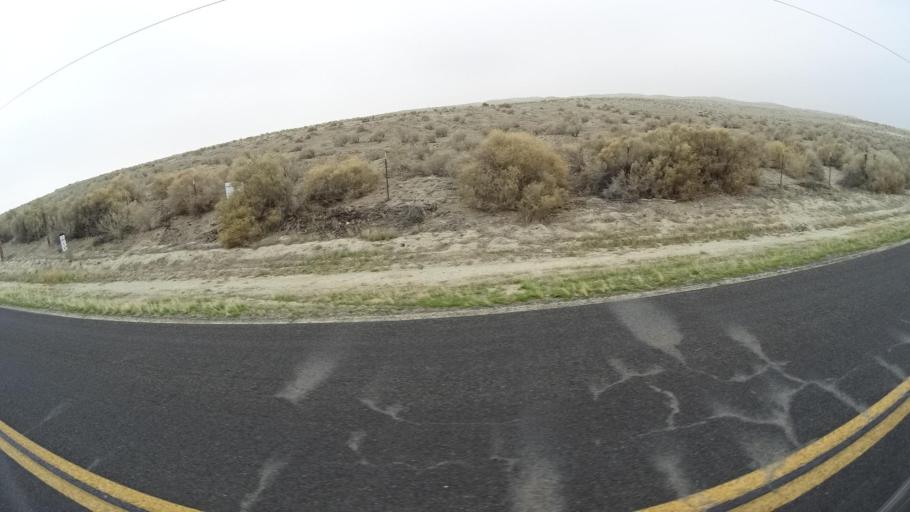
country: US
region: California
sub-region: Kern County
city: Ford City
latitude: 35.2443
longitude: -119.3039
